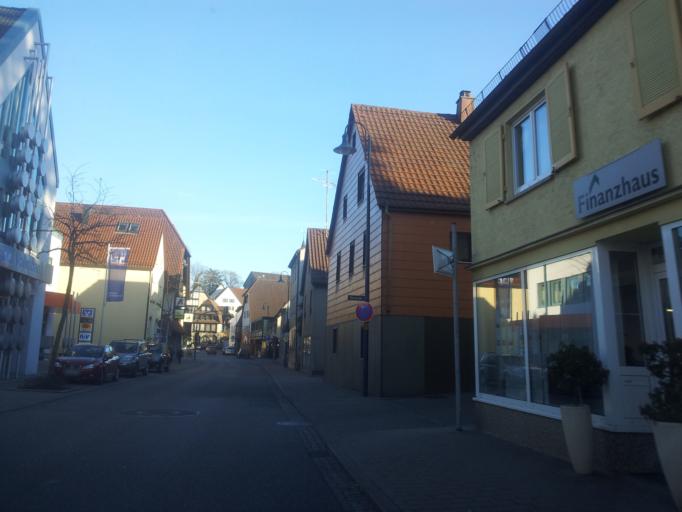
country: DE
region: Baden-Wuerttemberg
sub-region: Regierungsbezirk Stuttgart
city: Flein
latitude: 49.1016
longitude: 9.2119
